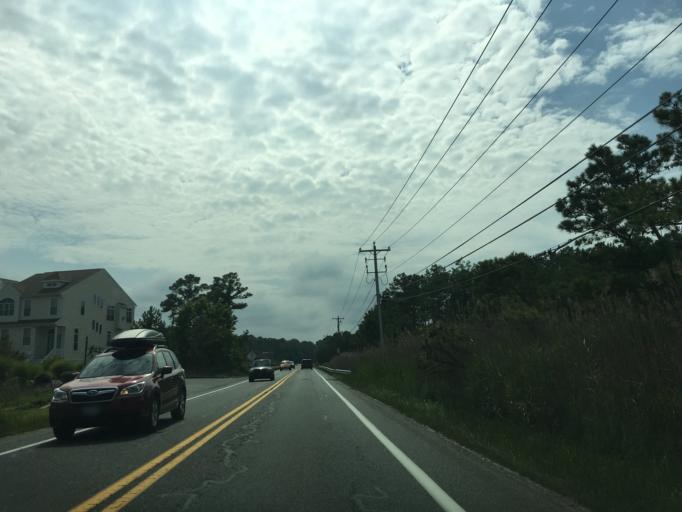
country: US
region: Delaware
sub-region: Sussex County
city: Bethany Beach
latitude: 38.5557
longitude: -75.0623
